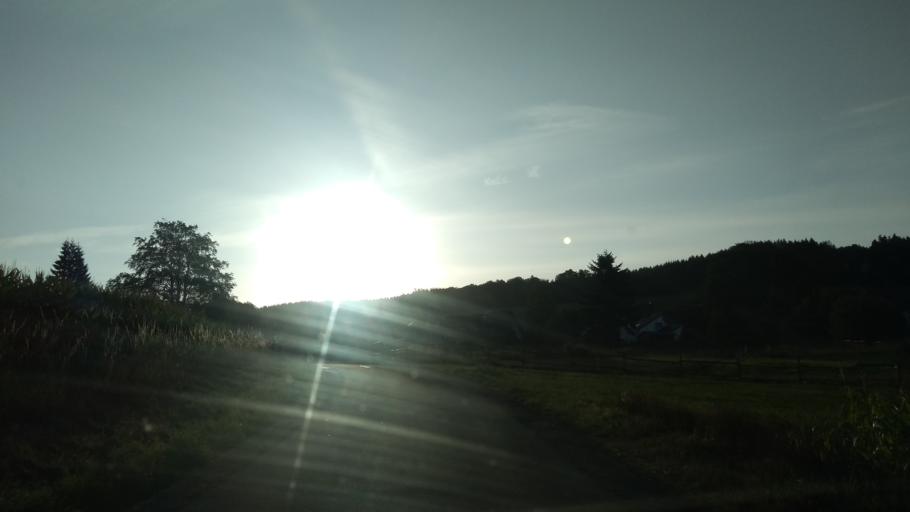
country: DE
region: North Rhine-Westphalia
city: Meinerzhagen
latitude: 51.0995
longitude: 7.6947
